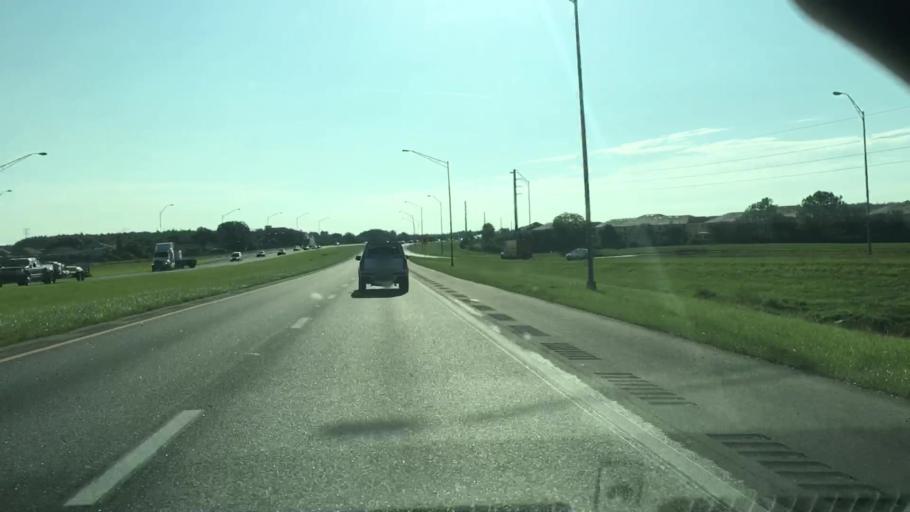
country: US
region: Florida
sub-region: Orange County
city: Meadow Woods
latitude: 28.3689
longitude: -81.3639
